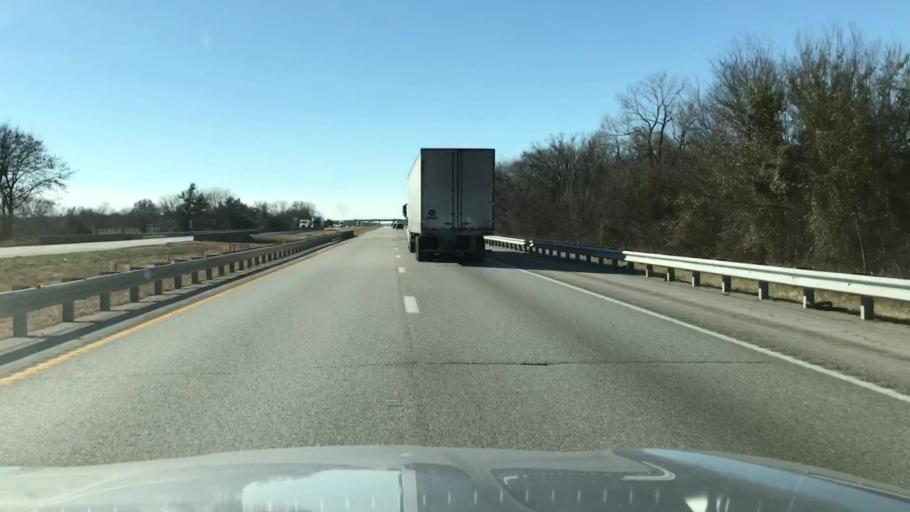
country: US
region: Missouri
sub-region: Jasper County
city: Duenweg
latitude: 37.0730
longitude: -94.3935
